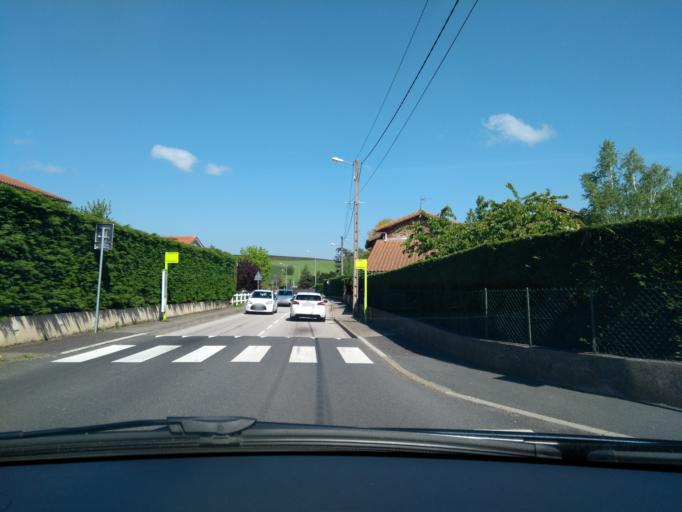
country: FR
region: Rhone-Alpes
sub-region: Departement de la Loire
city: Villars
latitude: 45.4648
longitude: 4.3443
